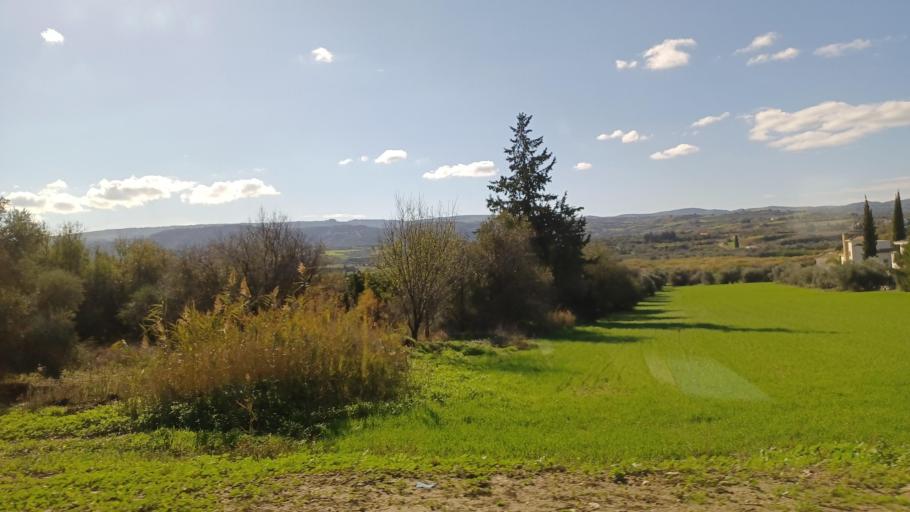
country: CY
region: Pafos
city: Polis
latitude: 35.0270
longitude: 32.4318
